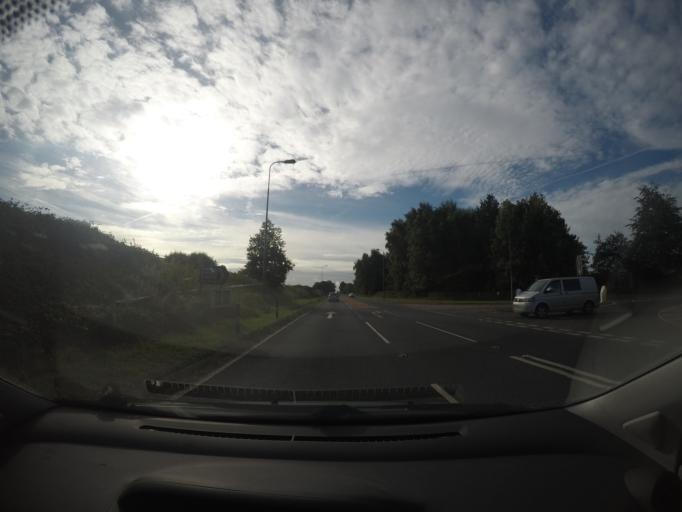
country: GB
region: England
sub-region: North Yorkshire
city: Riccall
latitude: 53.8298
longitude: -1.0518
